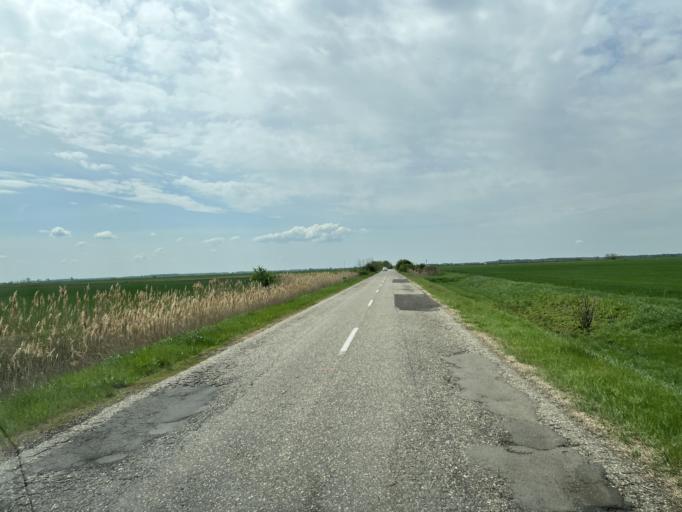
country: HU
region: Pest
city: Tortel
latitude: 47.1478
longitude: 19.9615
